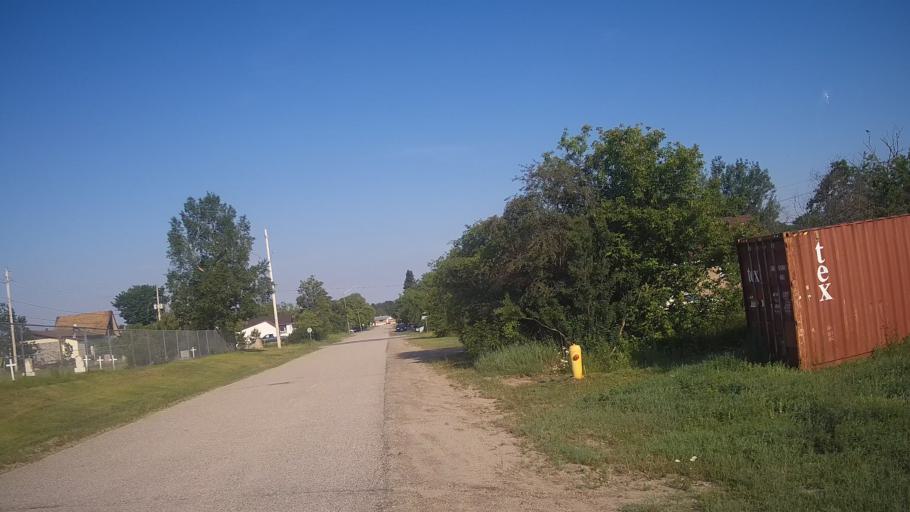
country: CA
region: Ontario
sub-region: Rainy River District
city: Atikokan
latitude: 49.4172
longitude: -91.6575
